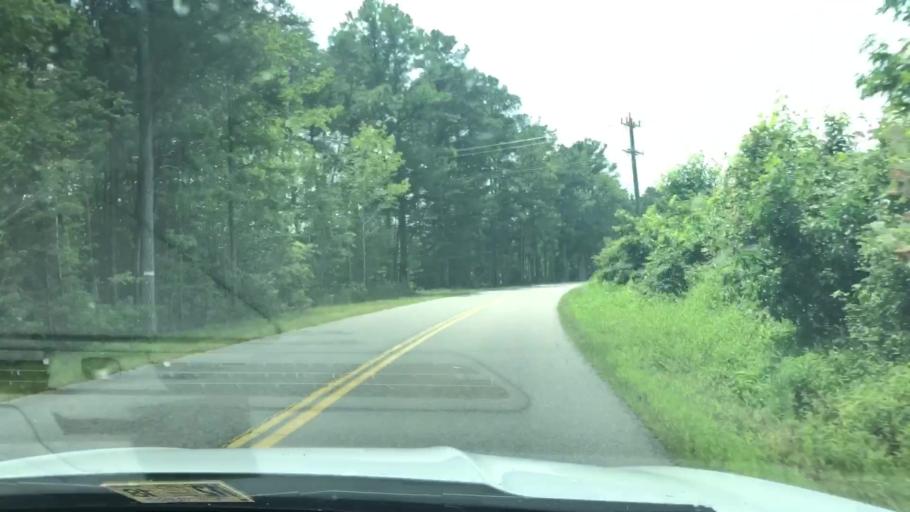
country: US
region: Virginia
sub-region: Middlesex County
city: Saluda
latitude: 37.6179
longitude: -76.7024
